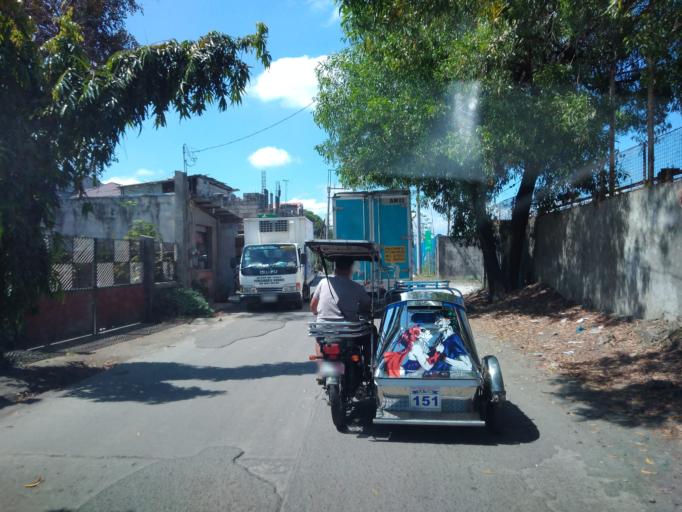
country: PH
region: Central Luzon
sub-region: Province of Bulacan
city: Bitungol
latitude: 14.8581
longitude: 121.0471
